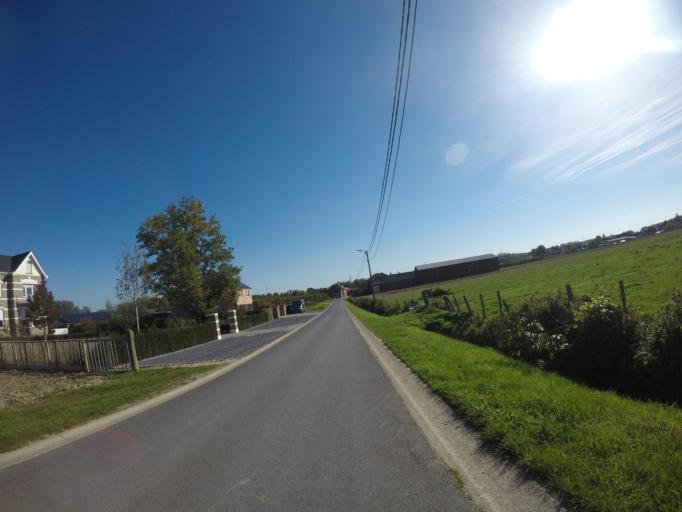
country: BE
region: Flanders
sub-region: Provincie Limburg
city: Alken
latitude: 50.8782
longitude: 5.2781
